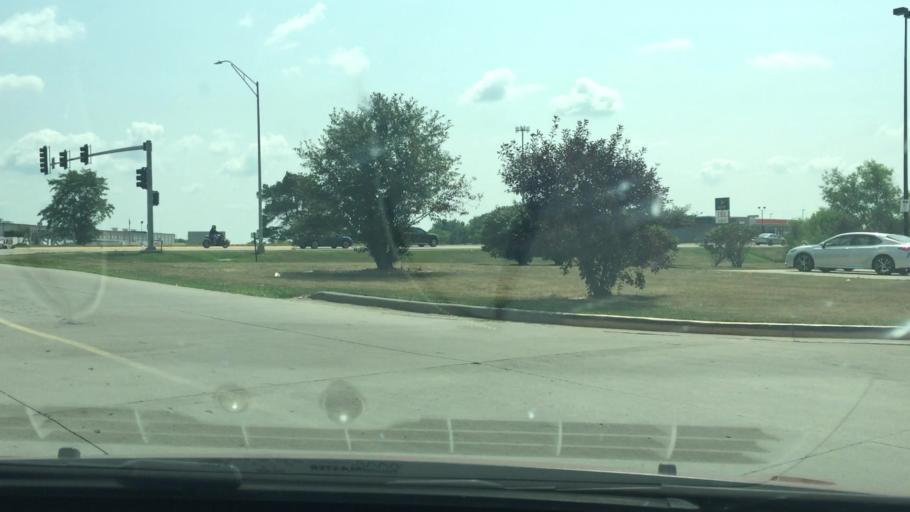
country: US
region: Iowa
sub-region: Muscatine County
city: Muscatine
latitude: 41.4565
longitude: -91.0248
